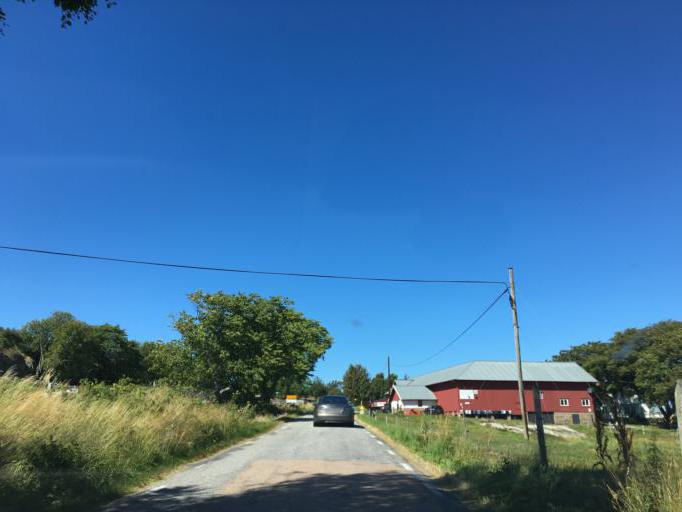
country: SE
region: Vaestra Goetaland
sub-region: Sotenas Kommun
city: Hunnebostrand
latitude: 58.4274
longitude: 11.2658
